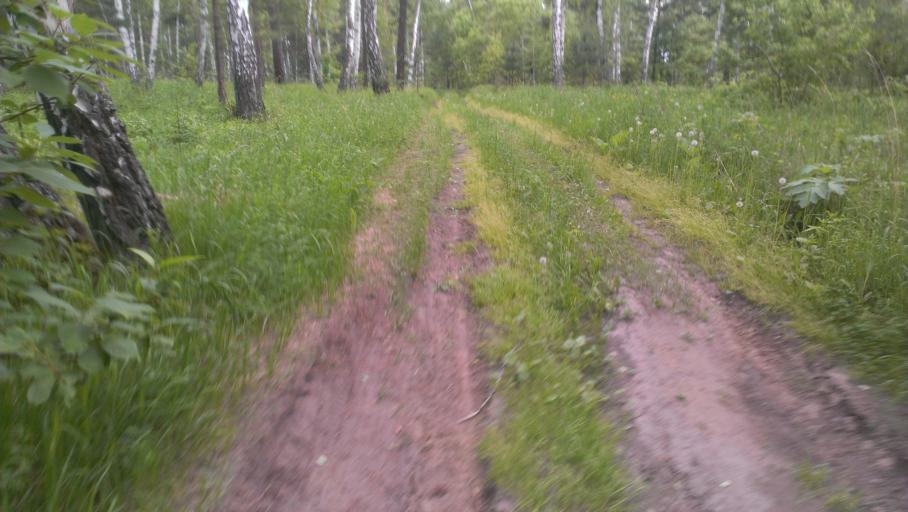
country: RU
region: Altai Krai
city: Sannikovo
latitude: 53.3393
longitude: 84.0494
